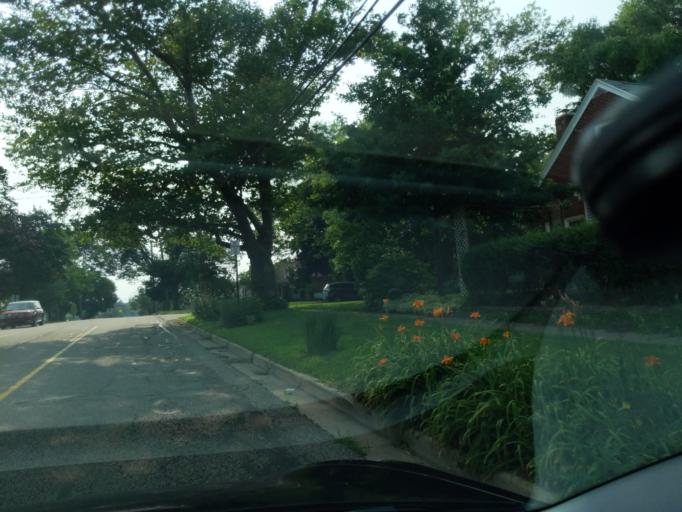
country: US
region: Michigan
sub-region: Jackson County
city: Jackson
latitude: 42.2401
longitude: -84.4302
